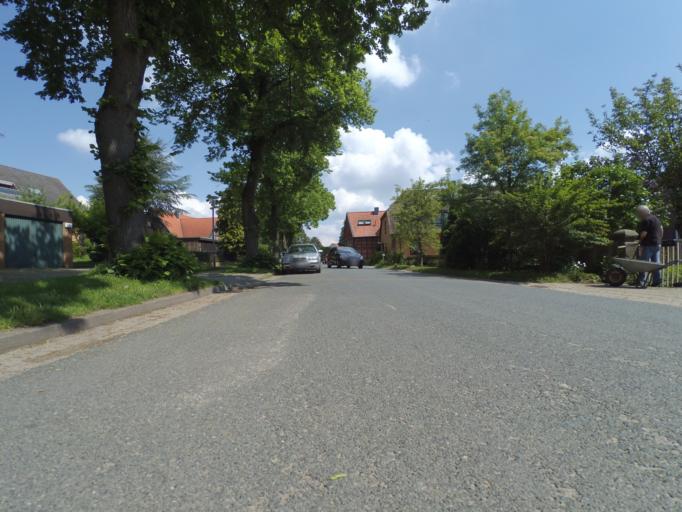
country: DE
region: Lower Saxony
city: Hohenhameln
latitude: 52.2567
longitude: 10.0699
